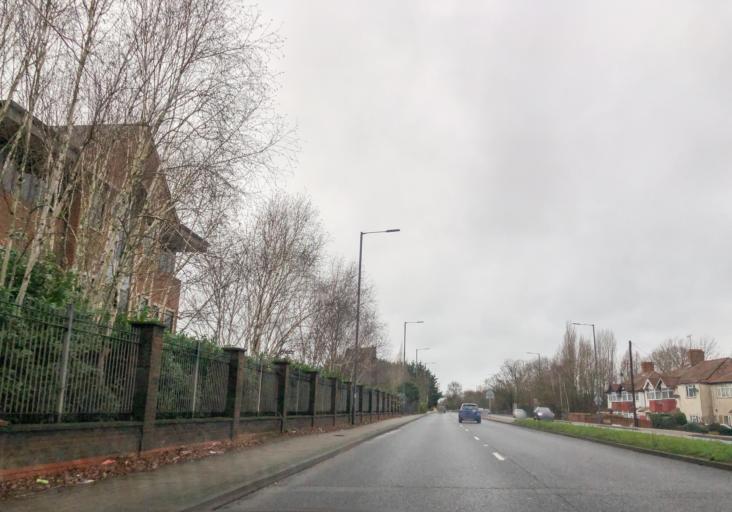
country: GB
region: England
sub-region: Greater London
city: West Drayton
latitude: 51.4825
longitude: -0.4831
